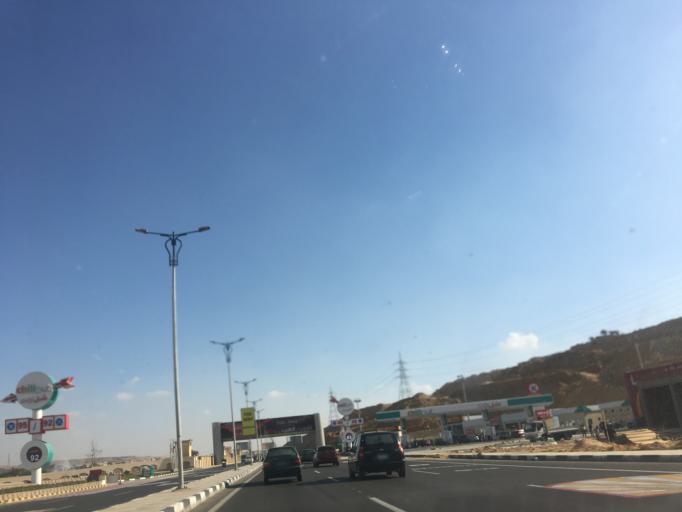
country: EG
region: Muhafazat al Qahirah
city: Cairo
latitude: 30.0221
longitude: 31.3284
